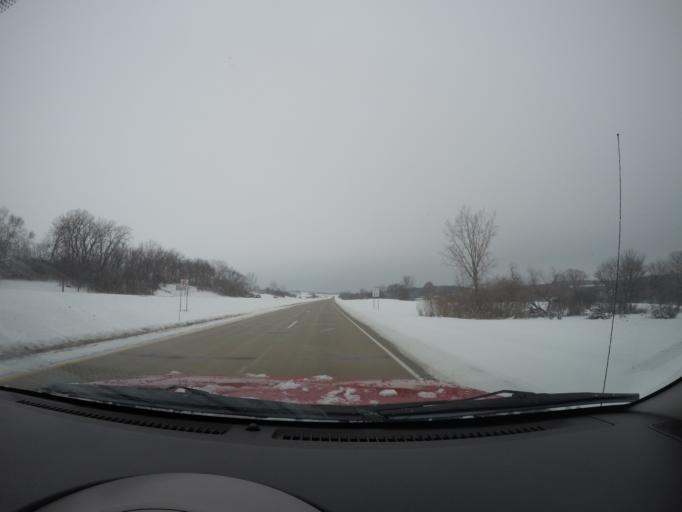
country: US
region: Minnesota
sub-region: Olmsted County
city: Rochester
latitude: 43.9621
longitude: -92.3869
